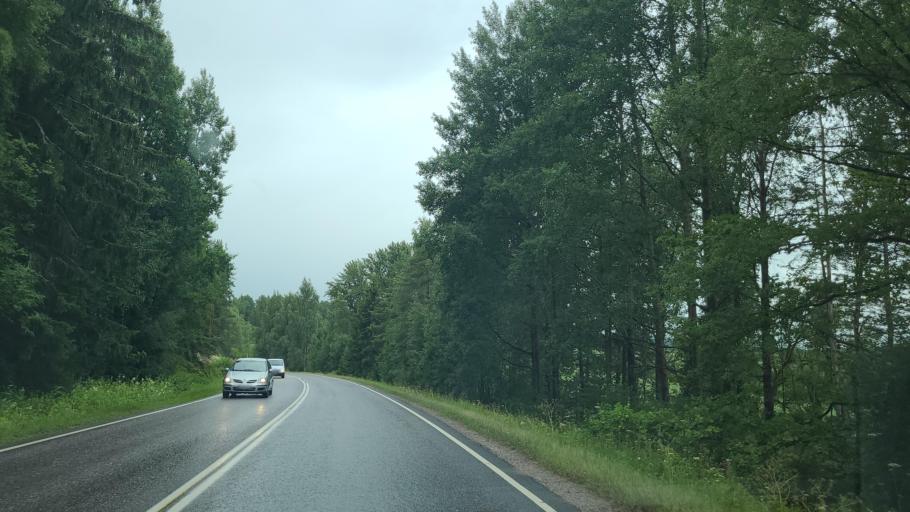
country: FI
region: Varsinais-Suomi
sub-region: Turku
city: Sauvo
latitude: 60.3024
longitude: 22.6816
